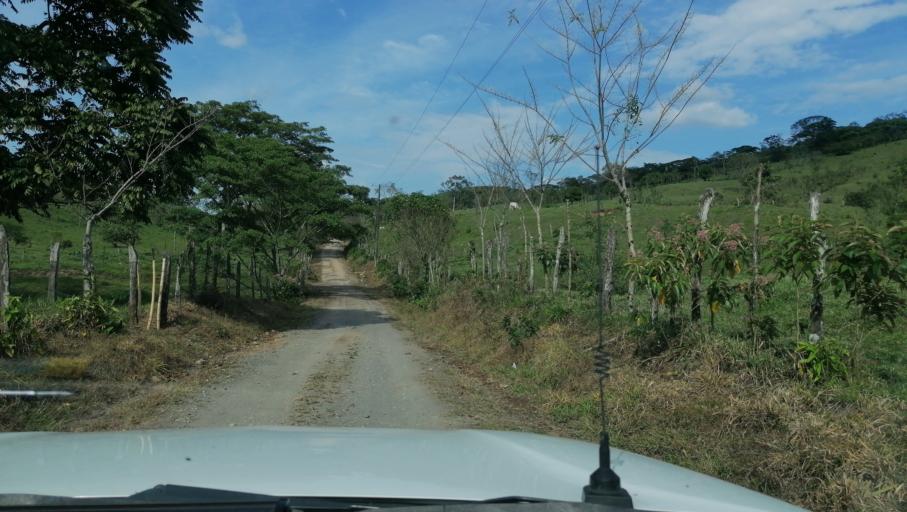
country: MX
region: Chiapas
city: Ostuacan
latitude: 17.4626
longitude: -93.2393
